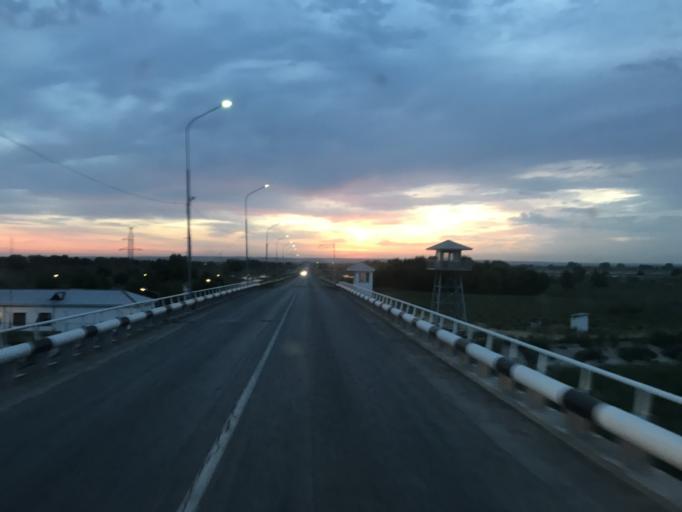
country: KZ
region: Ongtustik Qazaqstan
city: Ilyich
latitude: 41.0302
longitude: 68.5191
